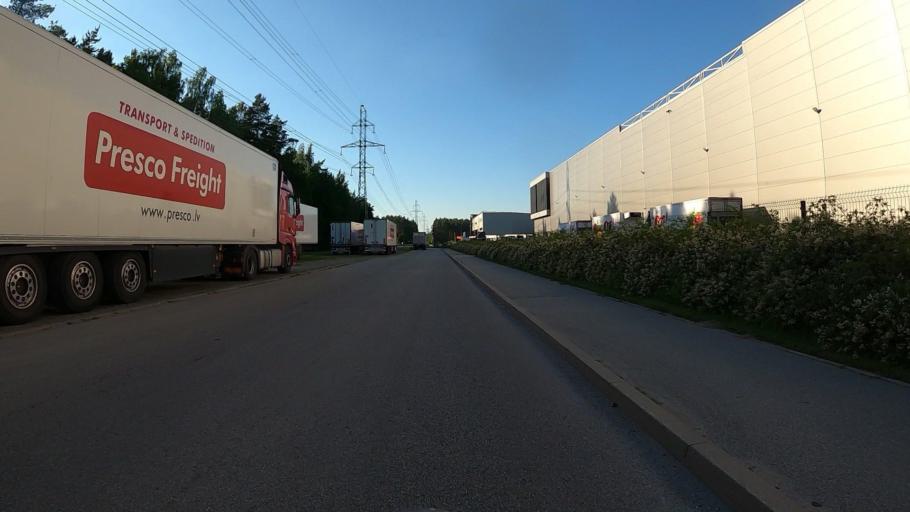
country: LV
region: Stopini
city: Ulbroka
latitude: 56.9348
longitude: 24.2357
